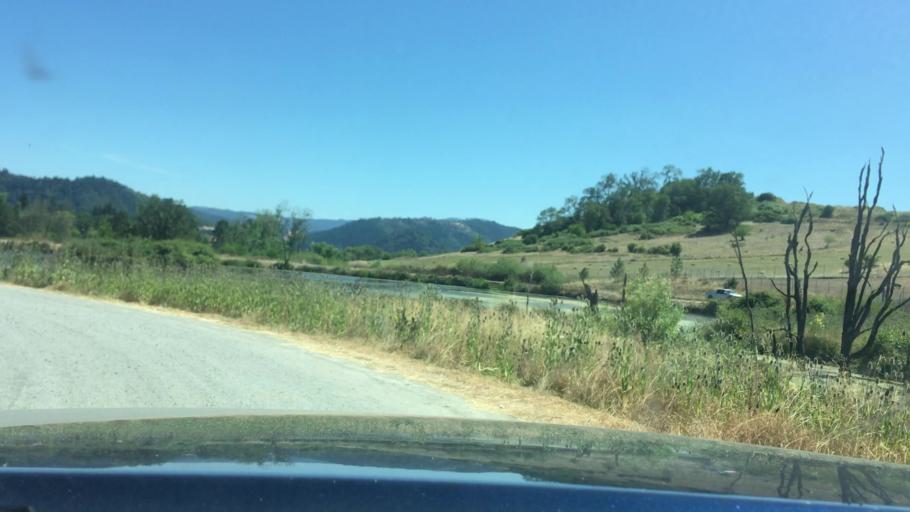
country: US
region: Oregon
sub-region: Douglas County
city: Winston
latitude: 43.1309
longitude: -123.4341
